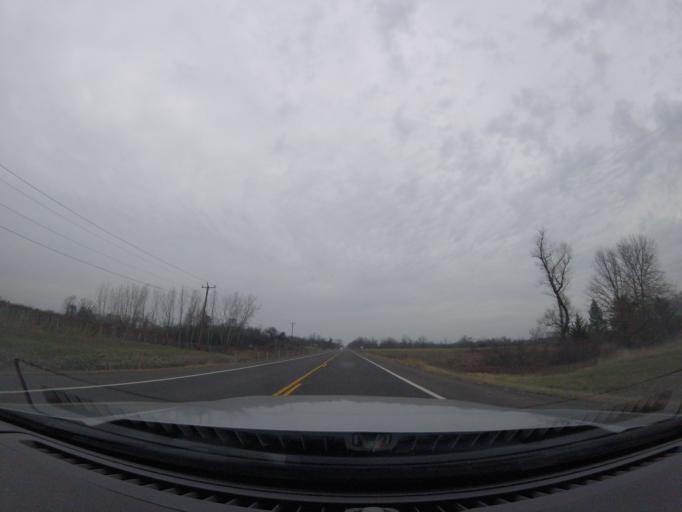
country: US
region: New York
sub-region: Yates County
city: Dundee
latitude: 42.6059
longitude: -76.9439
